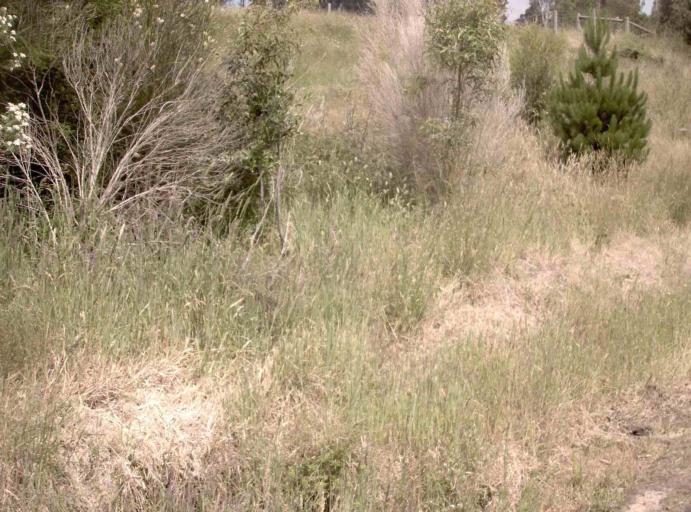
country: AU
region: Victoria
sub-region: Latrobe
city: Traralgon
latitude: -38.3272
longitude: 146.5741
